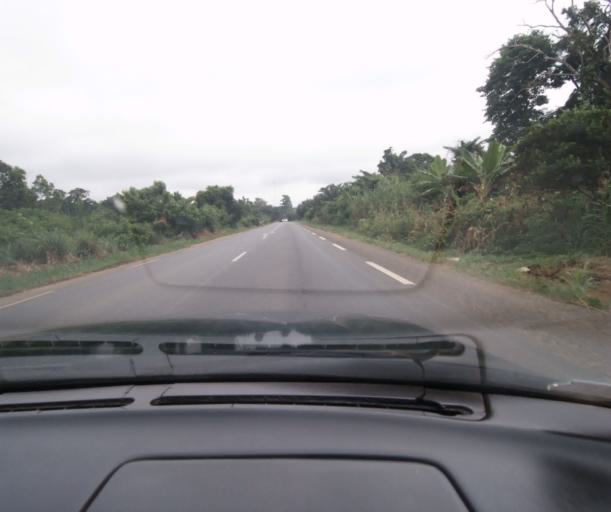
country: CM
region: Centre
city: Saa
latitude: 4.3350
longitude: 11.2848
